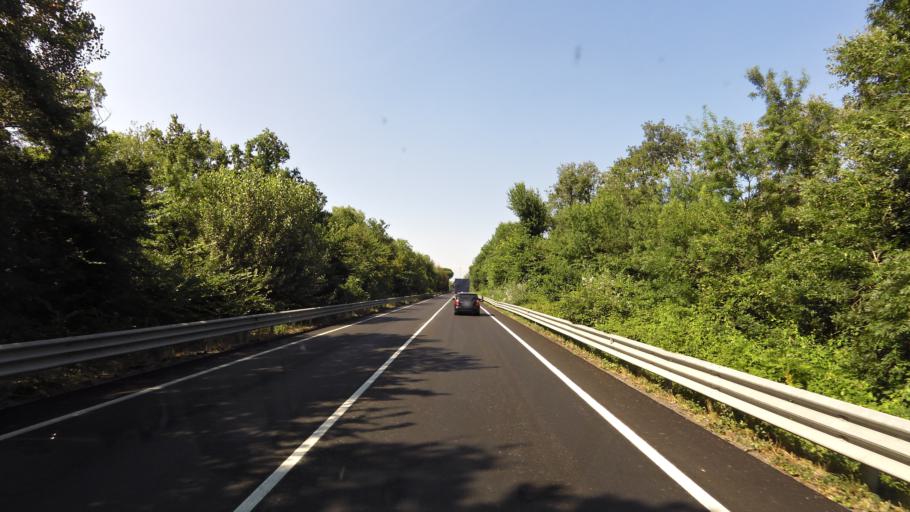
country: IT
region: Emilia-Romagna
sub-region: Provincia di Ravenna
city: Marina Romea
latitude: 44.5211
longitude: 12.2278
